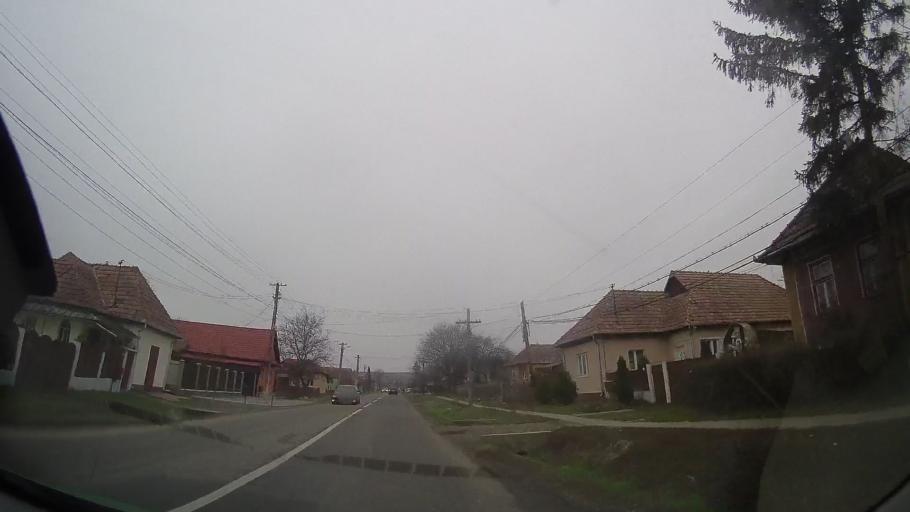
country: RO
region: Mures
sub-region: Comuna Ceausu de Campie
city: Ceausu de Campie
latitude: 46.6424
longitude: 24.5072
